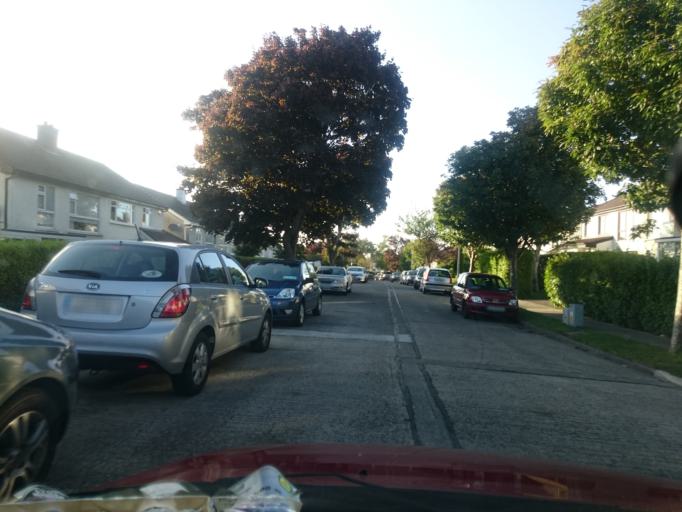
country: IE
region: Leinster
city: Balally
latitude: 53.2748
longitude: -6.2334
